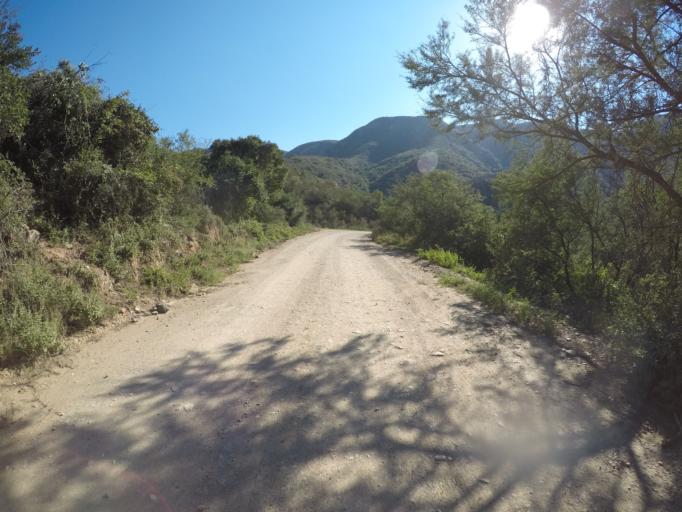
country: ZA
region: Eastern Cape
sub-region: Cacadu District Municipality
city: Kareedouw
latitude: -33.6582
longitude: 24.5260
